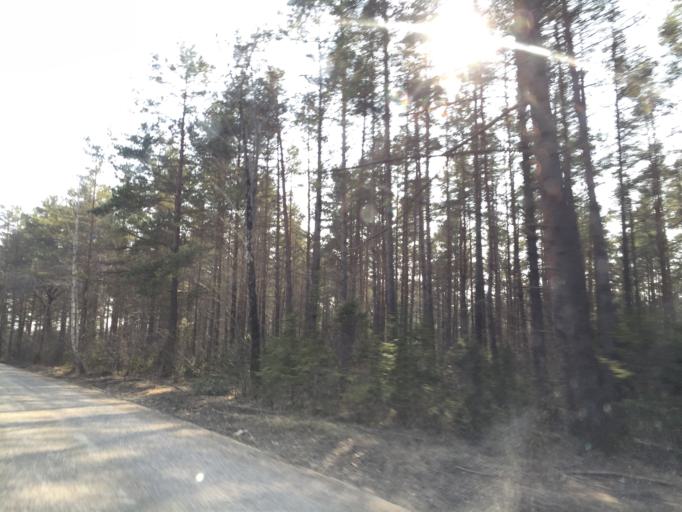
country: EE
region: Saare
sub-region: Orissaare vald
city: Orissaare
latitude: 58.5645
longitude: 23.2730
